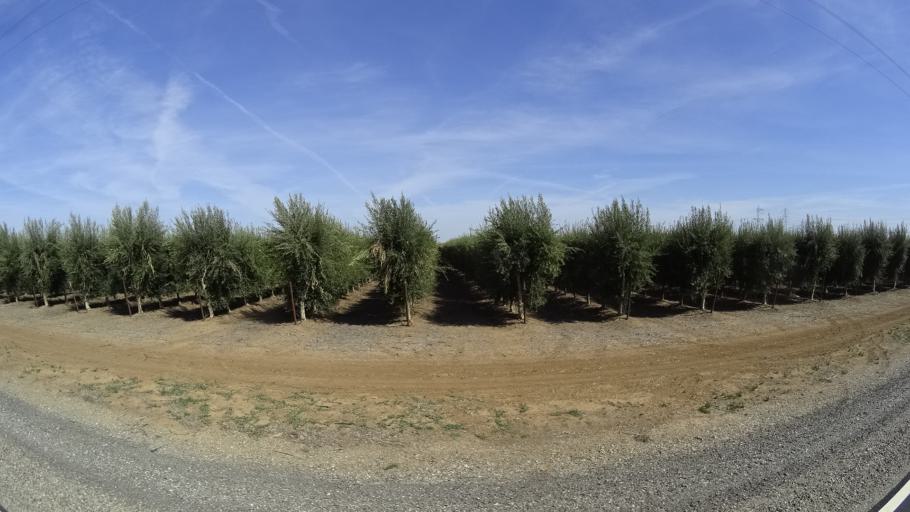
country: US
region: California
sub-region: Glenn County
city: Willows
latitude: 39.5241
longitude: -122.2898
